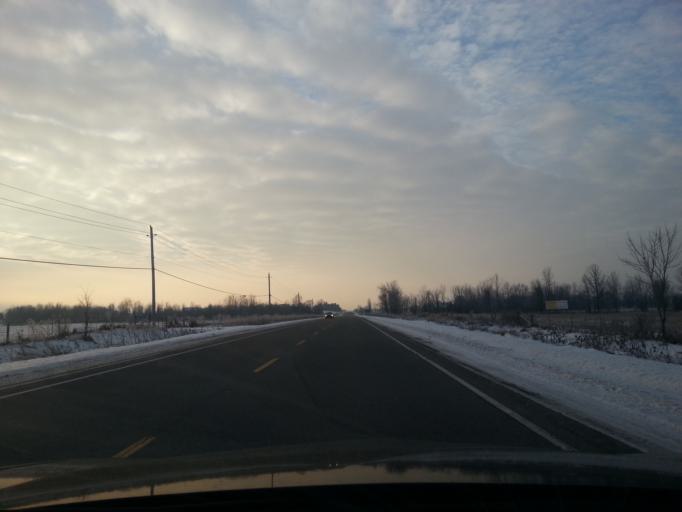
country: CA
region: Ontario
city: Perth
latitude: 45.0035
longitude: -76.2296
